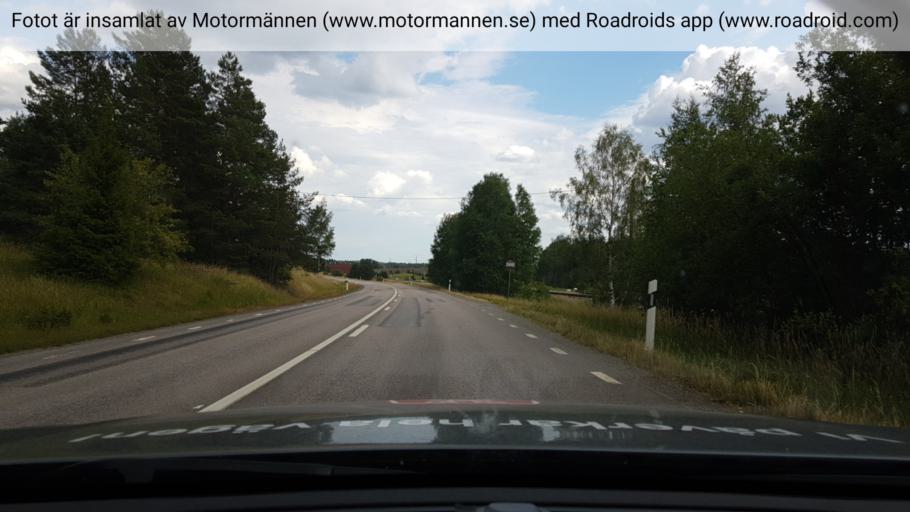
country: SE
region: Uppsala
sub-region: Heby Kommun
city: Morgongava
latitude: 59.9107
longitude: 17.0323
